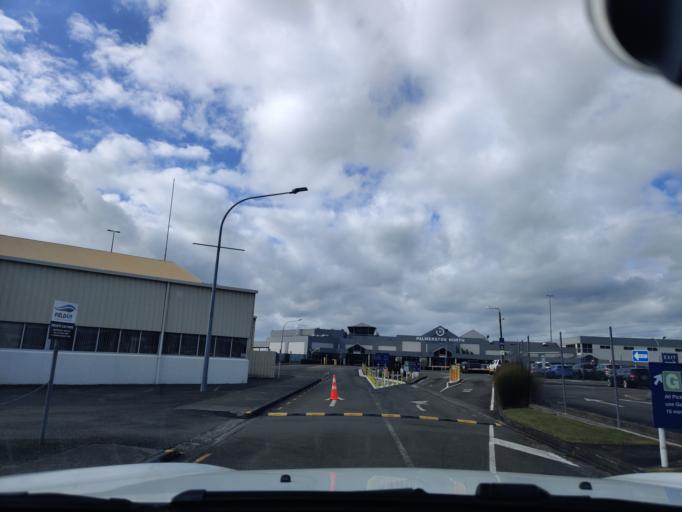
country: NZ
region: Manawatu-Wanganui
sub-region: Palmerston North City
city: Palmerston North
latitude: -40.3245
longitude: 175.6207
